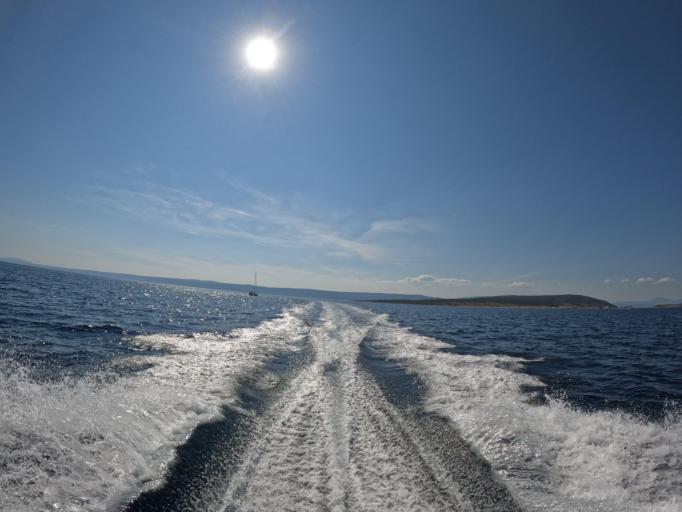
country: HR
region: Primorsko-Goranska
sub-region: Grad Krk
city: Krk
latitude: 44.9541
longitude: 14.5682
